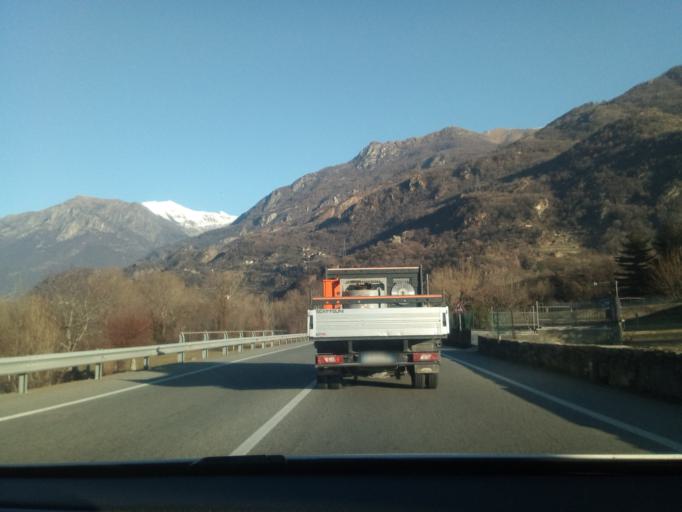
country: IT
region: Piedmont
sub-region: Provincia di Torino
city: Settimo Vittone
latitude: 45.5528
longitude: 7.8269
